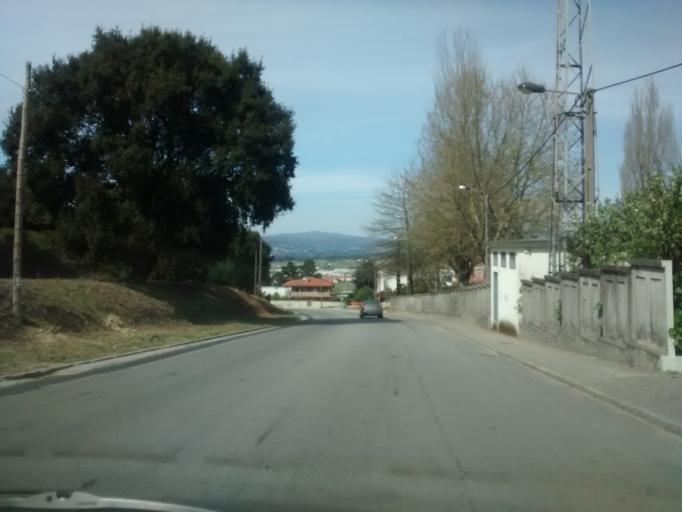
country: PT
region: Braga
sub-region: Braga
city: Braga
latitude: 41.5424
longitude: -8.4425
